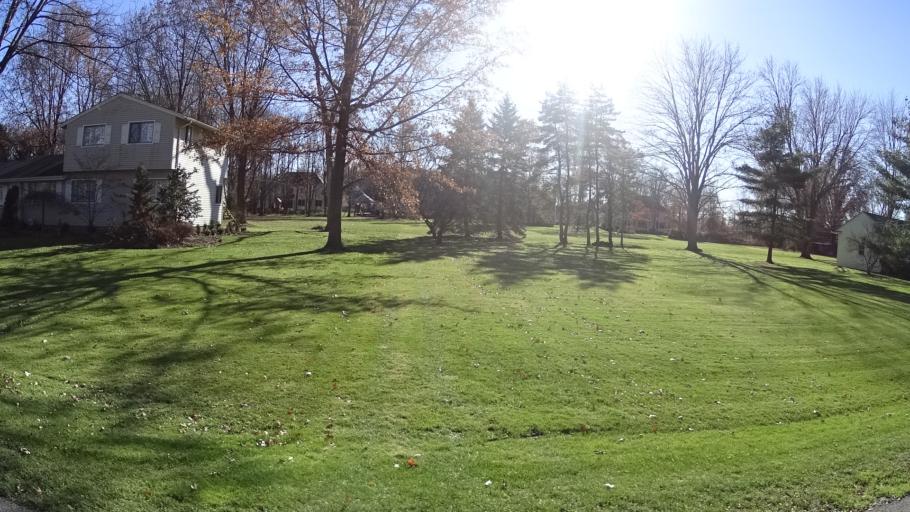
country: US
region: Ohio
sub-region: Lorain County
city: Avon Center
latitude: 41.4344
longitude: -81.9880
